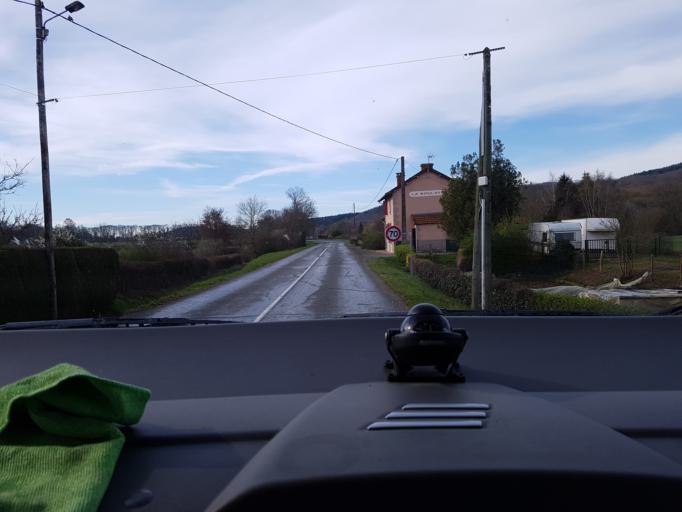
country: FR
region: Bourgogne
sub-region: Departement de Saone-et-Loire
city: Toulon-sur-Arroux
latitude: 46.7454
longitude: 4.1265
